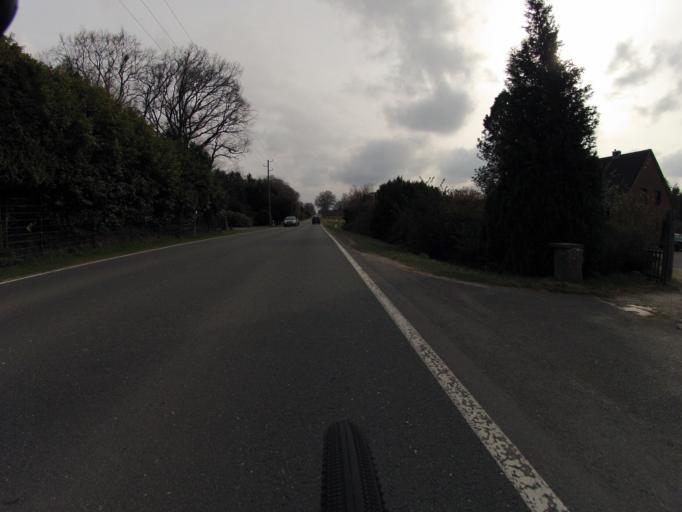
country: DE
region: North Rhine-Westphalia
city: Ibbenburen
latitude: 52.3143
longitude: 7.6956
